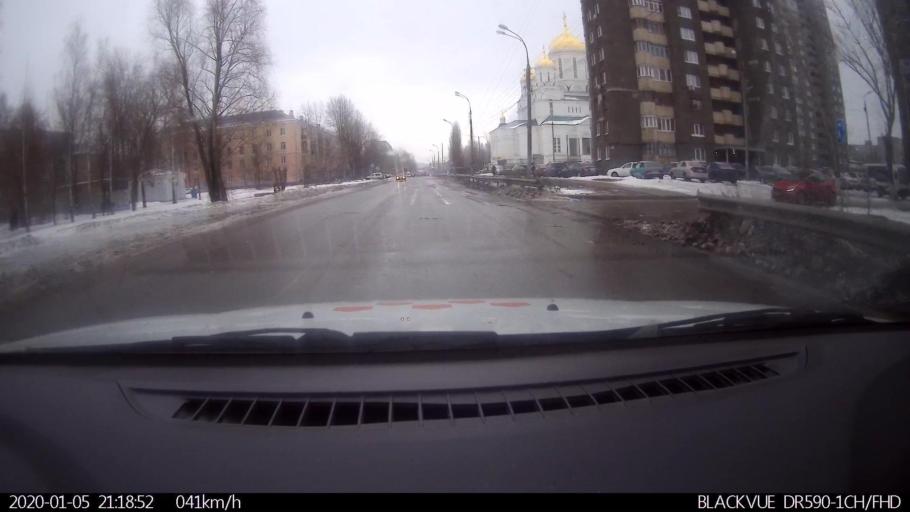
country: RU
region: Nizjnij Novgorod
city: Gorbatovka
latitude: 56.2640
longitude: 43.8782
